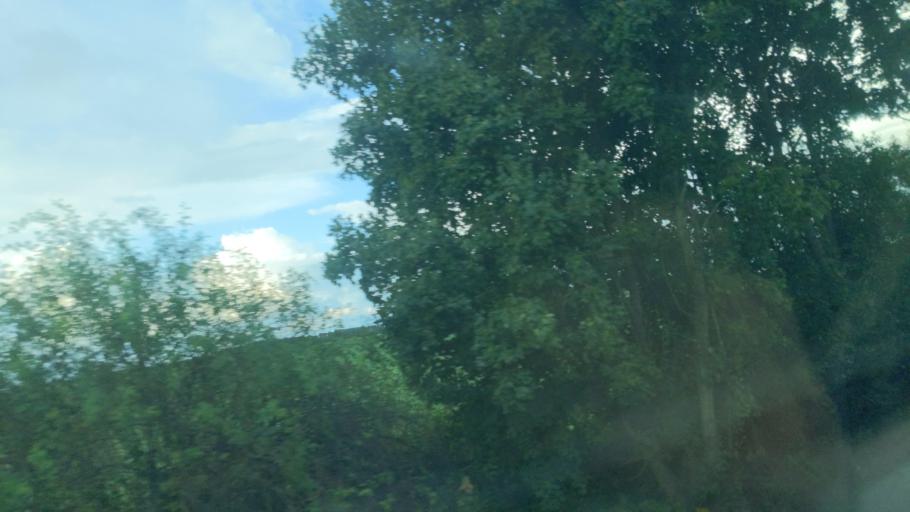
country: CZ
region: Central Bohemia
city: Uvaly
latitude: 50.0764
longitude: 14.7582
